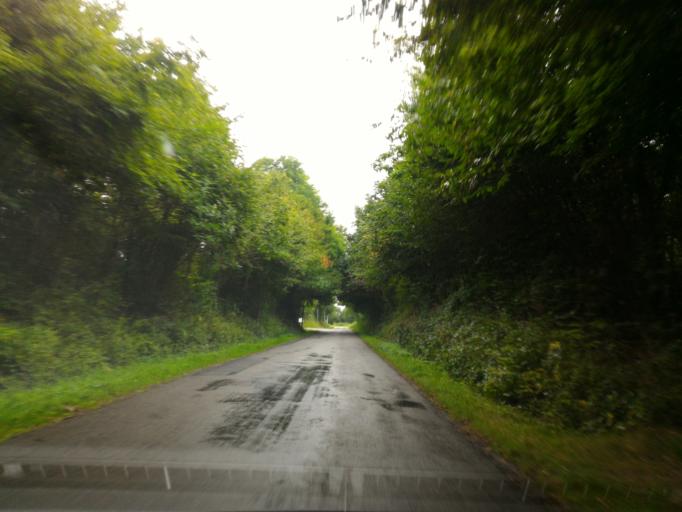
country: FR
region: Poitou-Charentes
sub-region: Departement de la Charente
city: Etagnac
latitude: 45.9346
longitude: 0.7873
